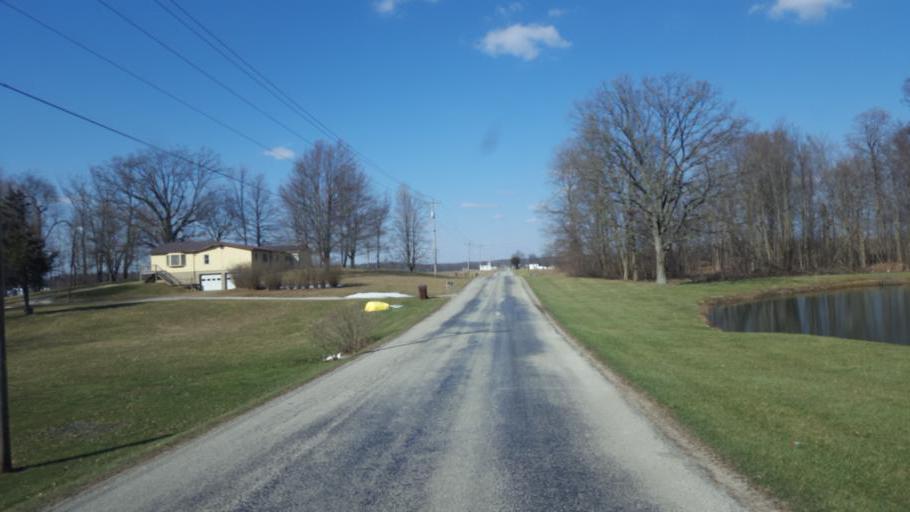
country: US
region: Ohio
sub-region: Morrow County
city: Mount Gilead
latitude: 40.4882
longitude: -82.7518
